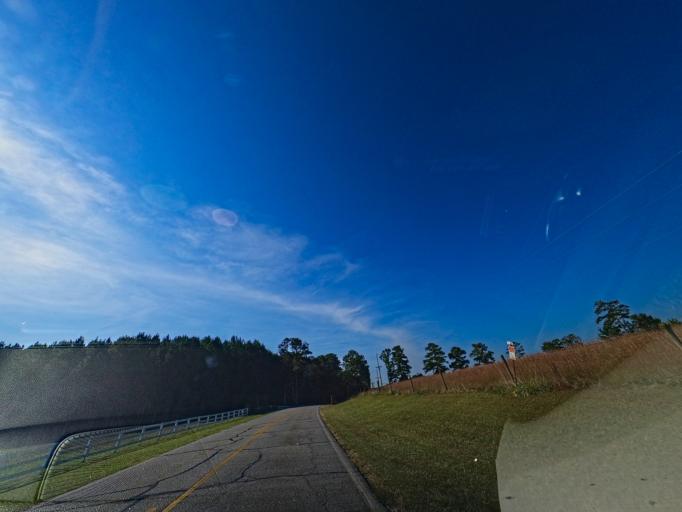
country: US
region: Georgia
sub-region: Coweta County
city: Grantville
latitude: 33.2963
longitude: -84.9291
